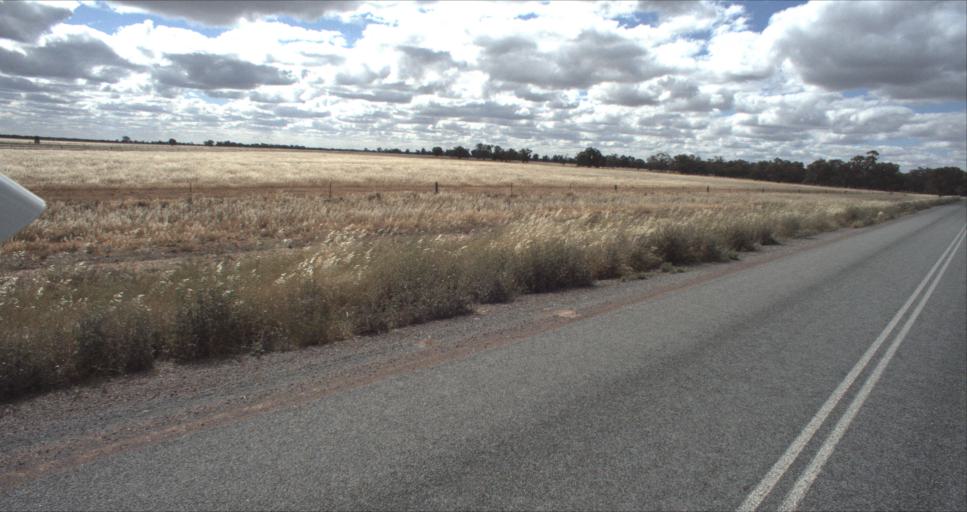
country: AU
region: New South Wales
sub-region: Leeton
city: Leeton
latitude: -34.6959
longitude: 146.3428
